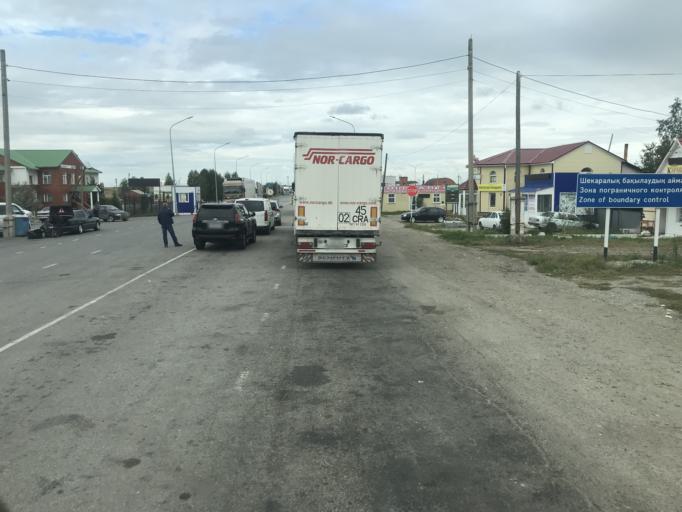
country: RU
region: Chelyabinsk
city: Bobrovka
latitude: 53.9983
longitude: 61.6424
